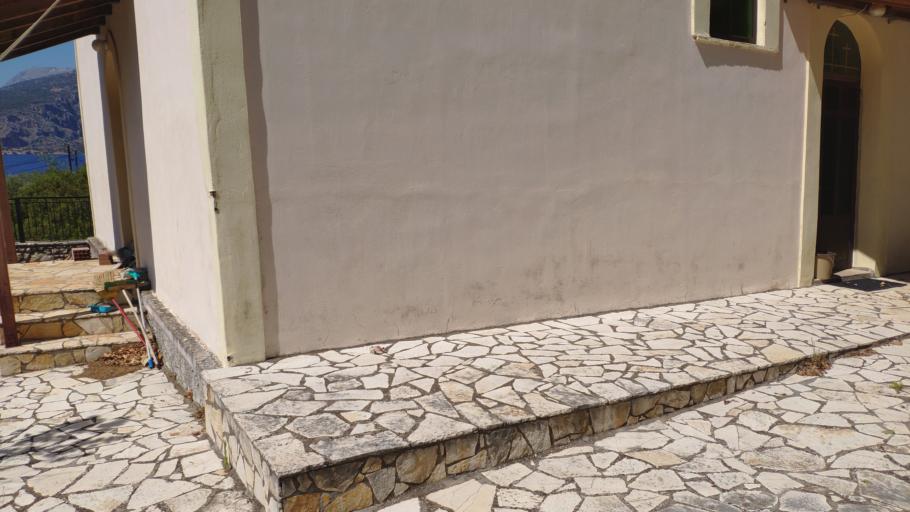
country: GR
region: West Greece
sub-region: Nomos Aitolias kai Akarnanias
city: Kandila
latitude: 38.6472
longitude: 20.9288
